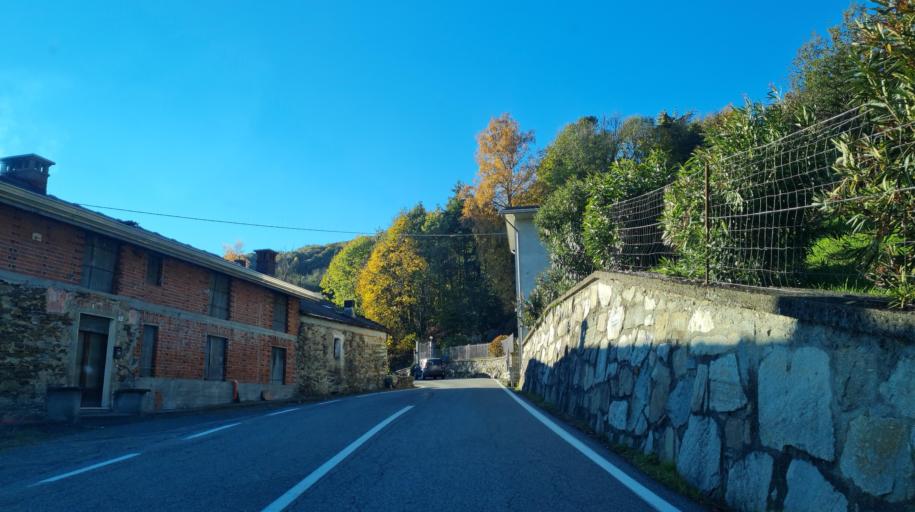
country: IT
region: Piedmont
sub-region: Provincia di Torino
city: Lessolo
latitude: 45.4664
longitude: 7.8003
